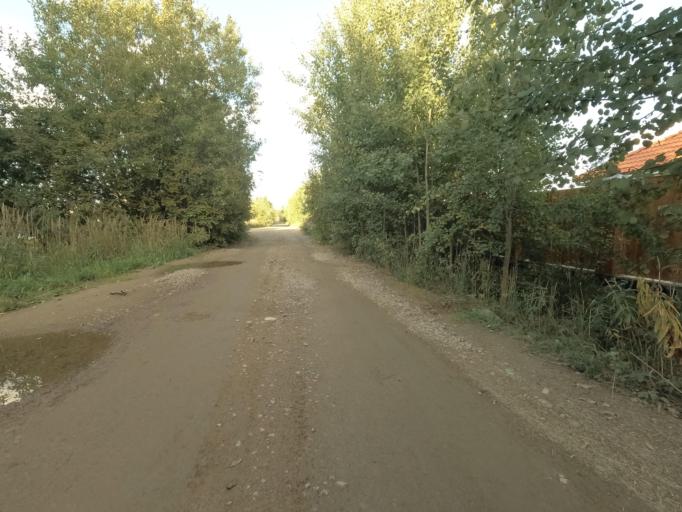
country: RU
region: Leningrad
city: Otradnoye
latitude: 59.8687
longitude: 30.7721
